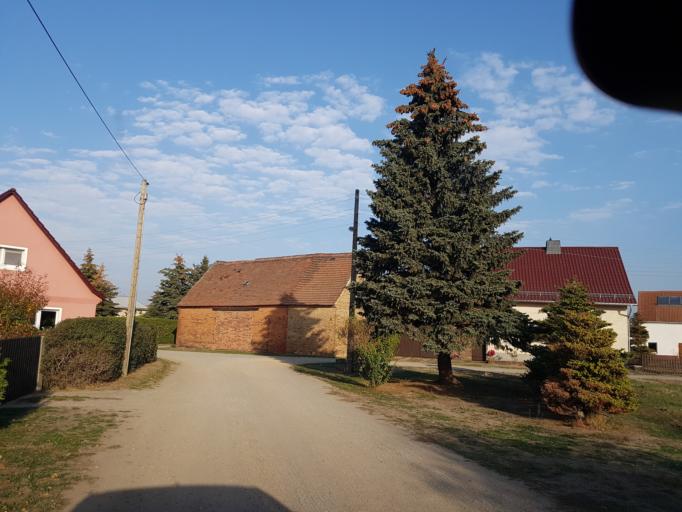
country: DE
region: Brandenburg
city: Finsterwalde
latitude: 51.6036
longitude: 13.6727
